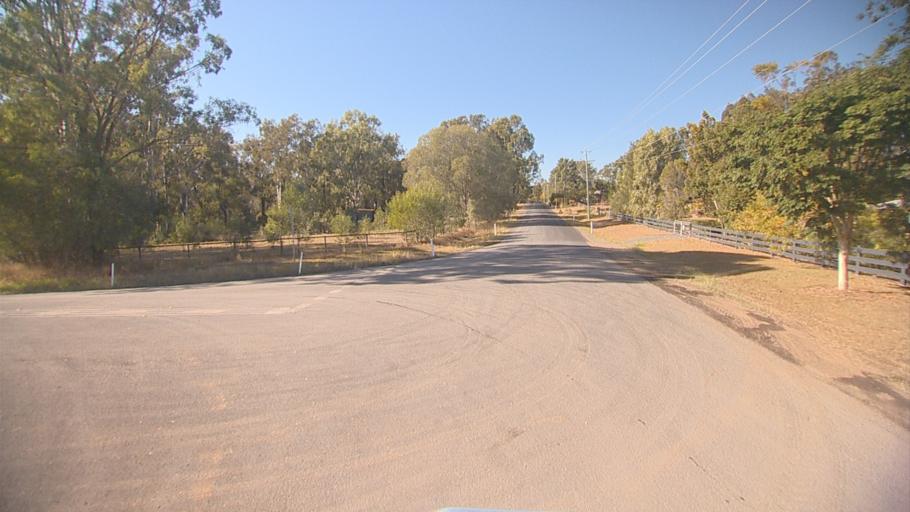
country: AU
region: Queensland
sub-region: Logan
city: Cedar Vale
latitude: -27.8360
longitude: 152.9943
